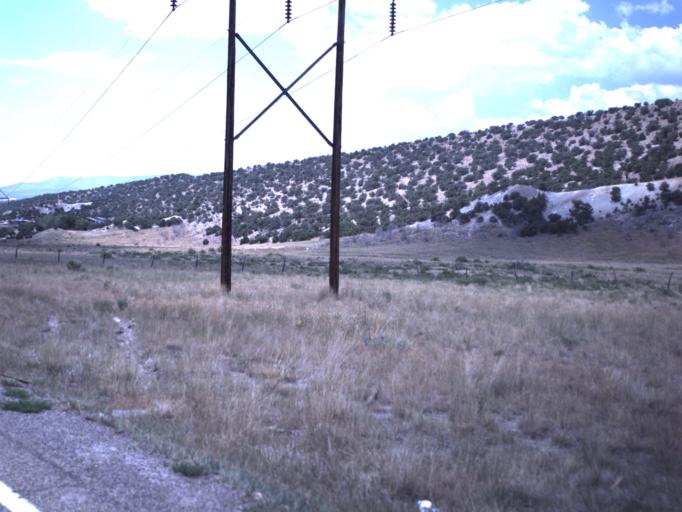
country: US
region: Utah
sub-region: Uintah County
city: Vernal
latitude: 40.5667
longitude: -109.4993
